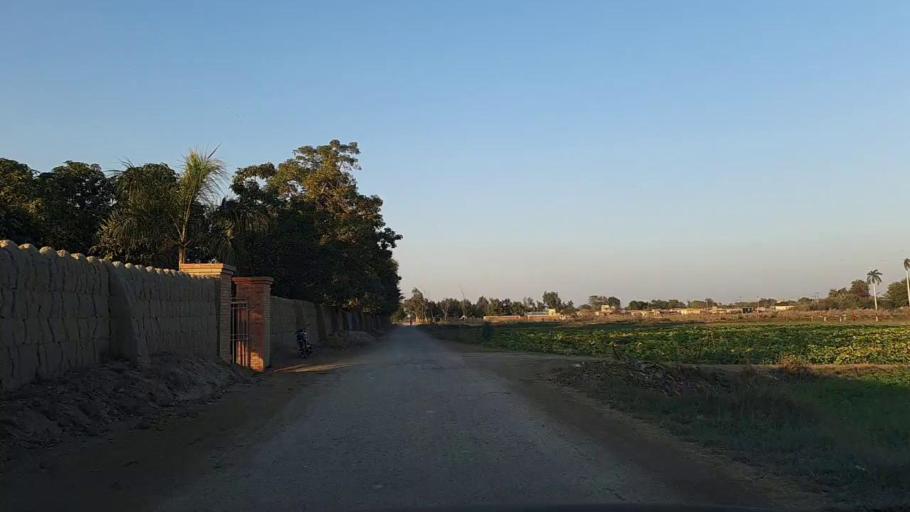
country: PK
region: Sindh
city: Nawabshah
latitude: 26.2446
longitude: 68.3384
